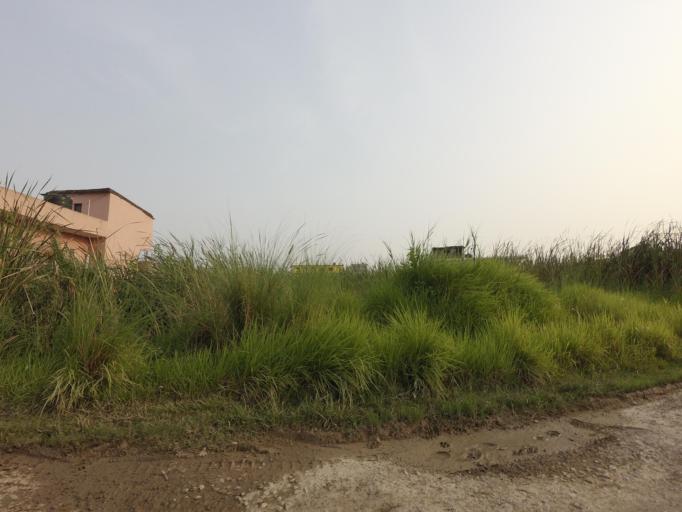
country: NP
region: Western Region
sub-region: Lumbini Zone
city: Bhairahawa
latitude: 27.5078
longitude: 83.4598
